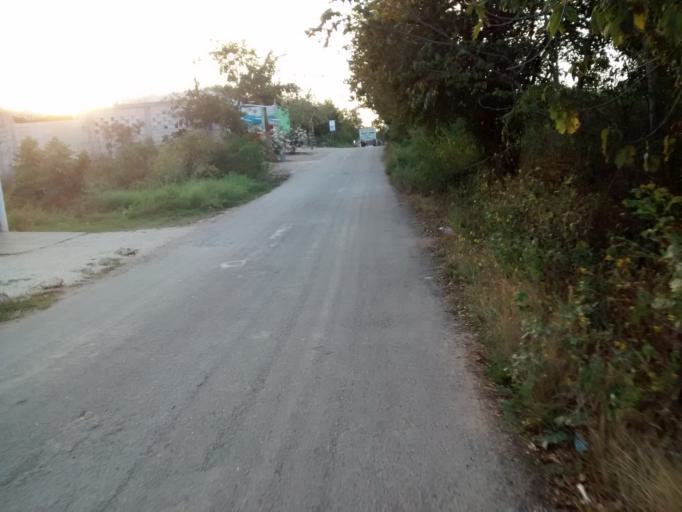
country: MX
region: Yucatan
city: Valladolid
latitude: 20.6842
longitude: -88.1770
